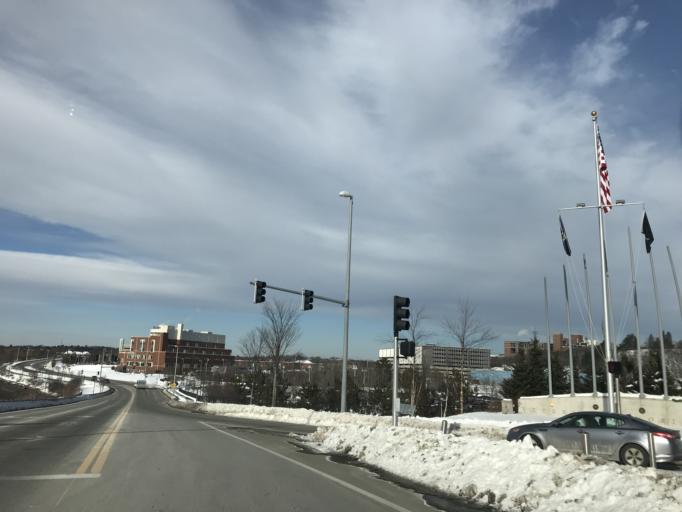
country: US
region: Maine
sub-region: Cumberland County
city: Portland
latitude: 43.6447
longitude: -70.2808
